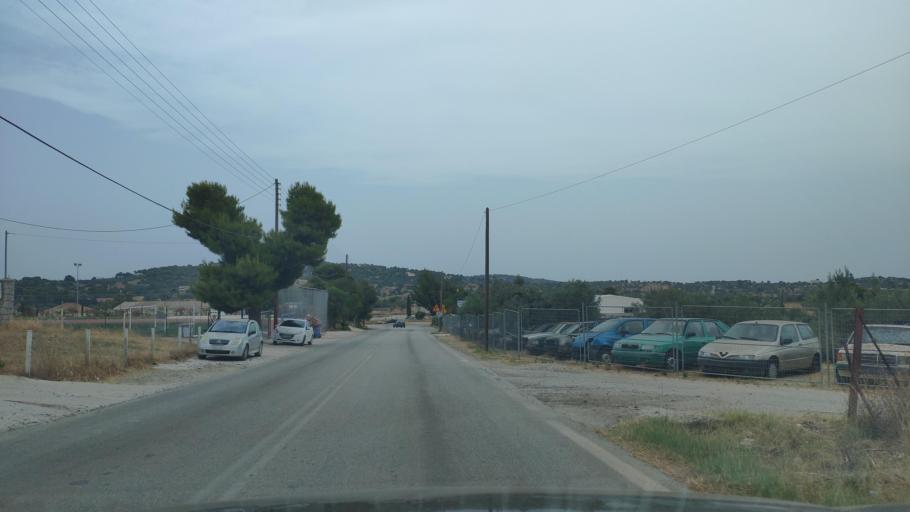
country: GR
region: Peloponnese
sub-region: Nomos Argolidos
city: Kranidi
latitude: 37.3708
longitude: 23.1601
